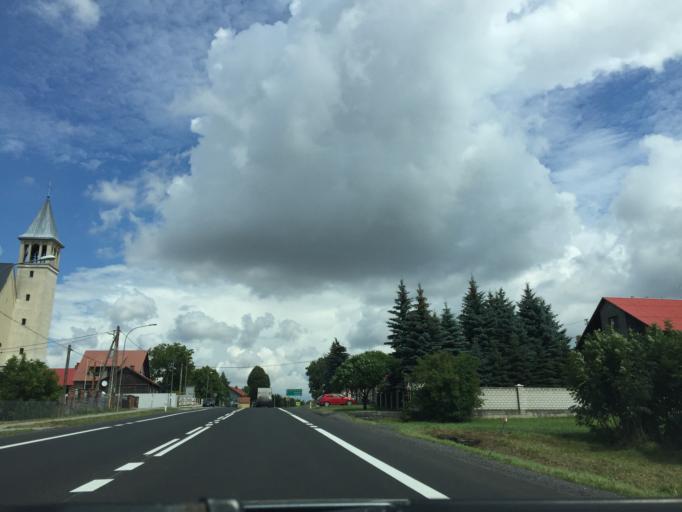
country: PL
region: Lesser Poland Voivodeship
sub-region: Powiat krakowski
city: Michalowice
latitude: 50.2020
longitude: 20.0116
